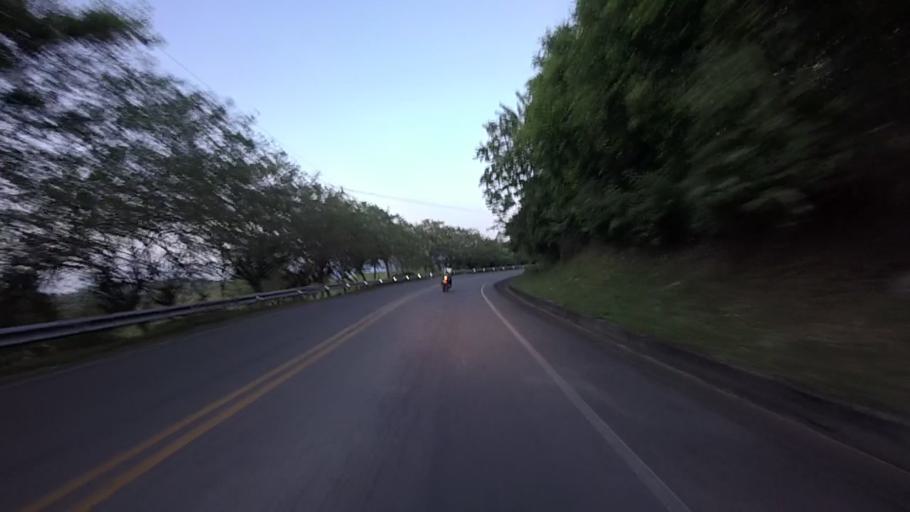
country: CO
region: Valle del Cauca
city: Cartago
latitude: 4.7276
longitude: -75.8907
